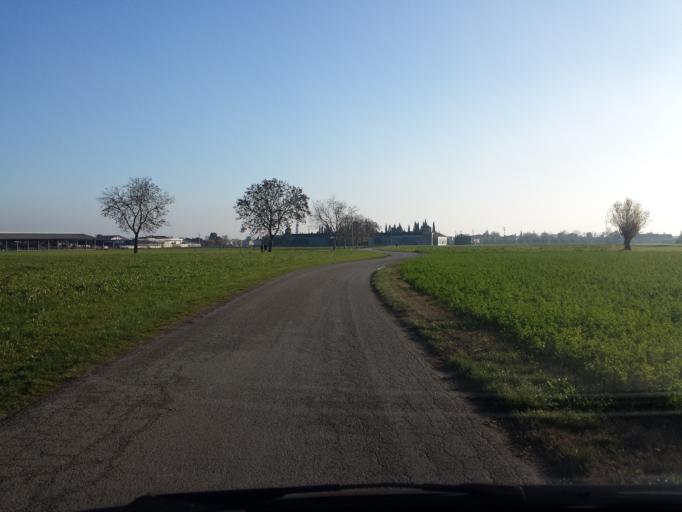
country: IT
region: Veneto
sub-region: Provincia di Vicenza
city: Sandrigo
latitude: 45.6729
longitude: 11.5923
